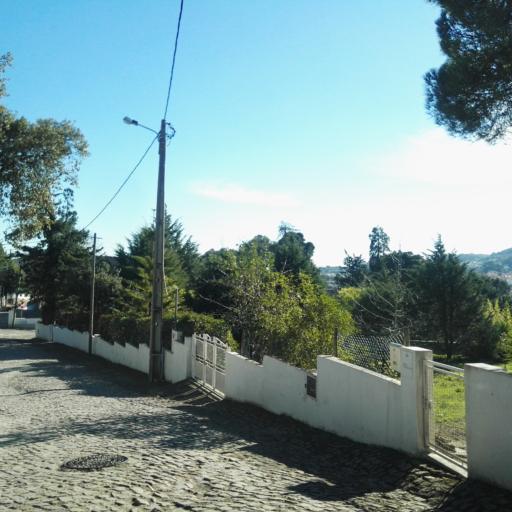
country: PT
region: Lisbon
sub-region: Mafra
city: Venda do Pinheiro
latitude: 38.9298
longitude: -9.2385
